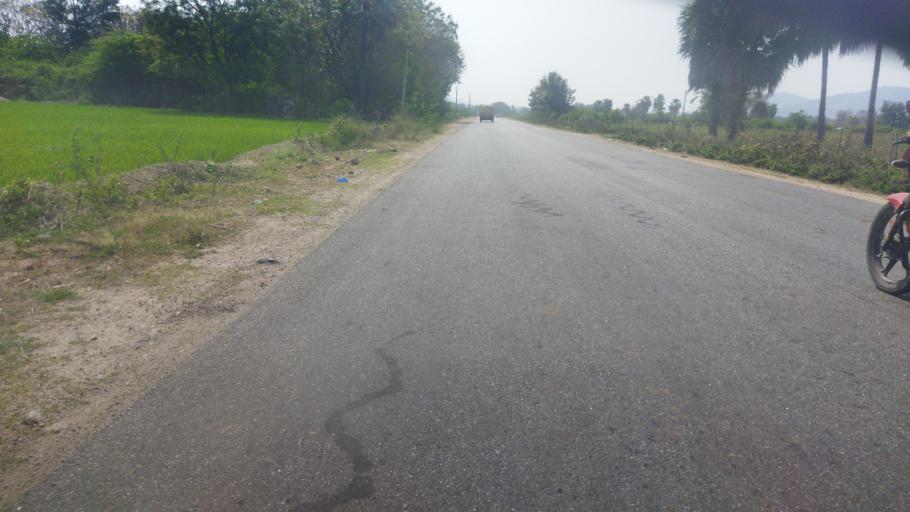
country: IN
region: Telangana
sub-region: Nalgonda
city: Nalgonda
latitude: 17.0904
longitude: 79.2852
